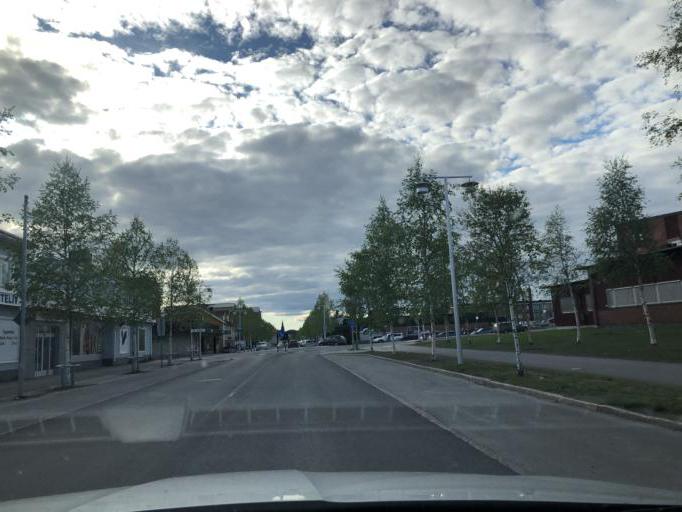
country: SE
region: Norrbotten
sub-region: Arvidsjaurs Kommun
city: Arvidsjaur
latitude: 65.5913
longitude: 19.1799
